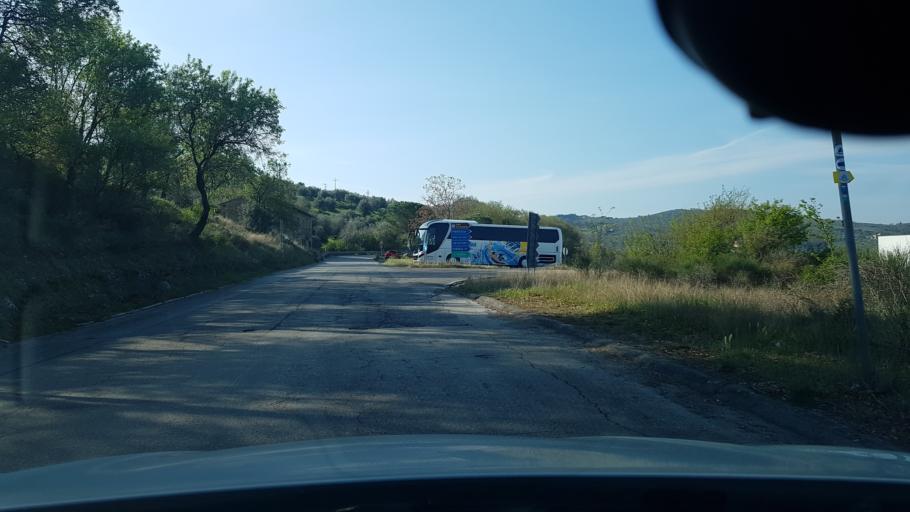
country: IT
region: Umbria
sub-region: Provincia di Perugia
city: Magione
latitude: 43.1655
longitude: 12.1896
